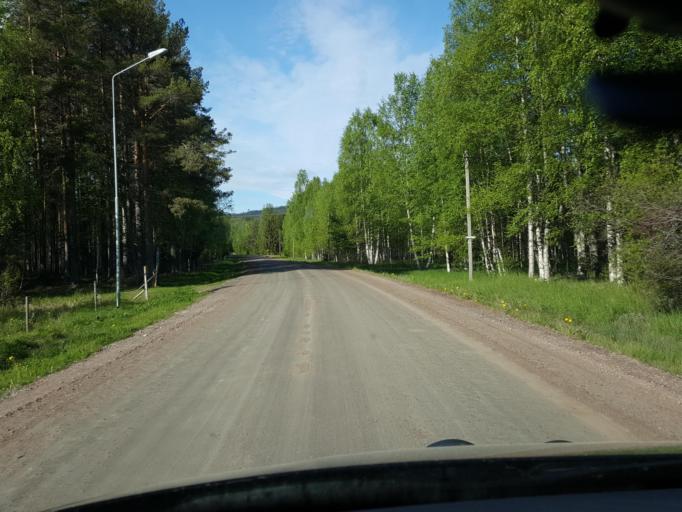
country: SE
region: Vaesternorrland
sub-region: Ange Kommun
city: Ange
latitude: 62.1832
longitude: 15.6373
